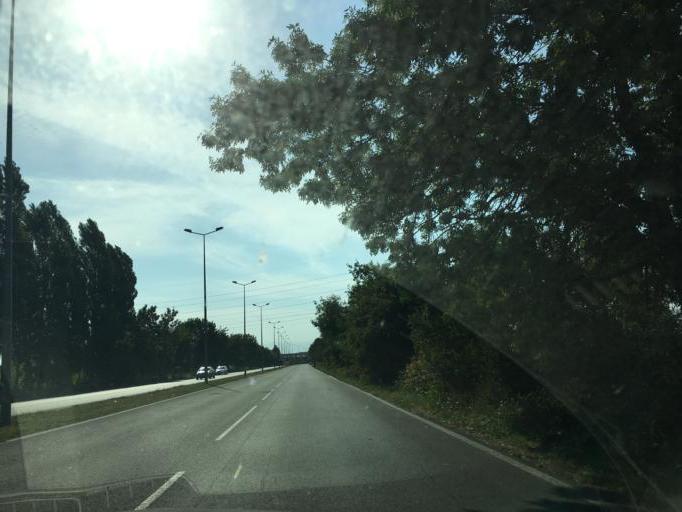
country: BG
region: Pazardzhik
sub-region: Obshtina Pazardzhik
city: Pazardzhik
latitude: 42.2157
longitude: 24.3187
